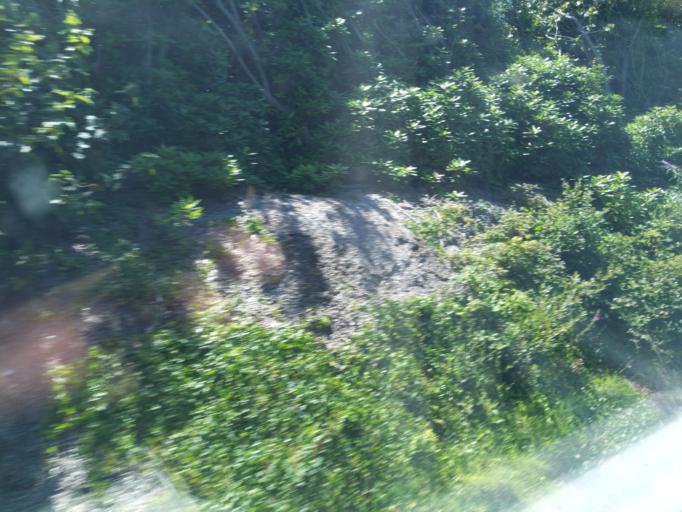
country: GB
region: England
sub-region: Cornwall
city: St Austell
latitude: 50.3403
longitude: -4.7925
